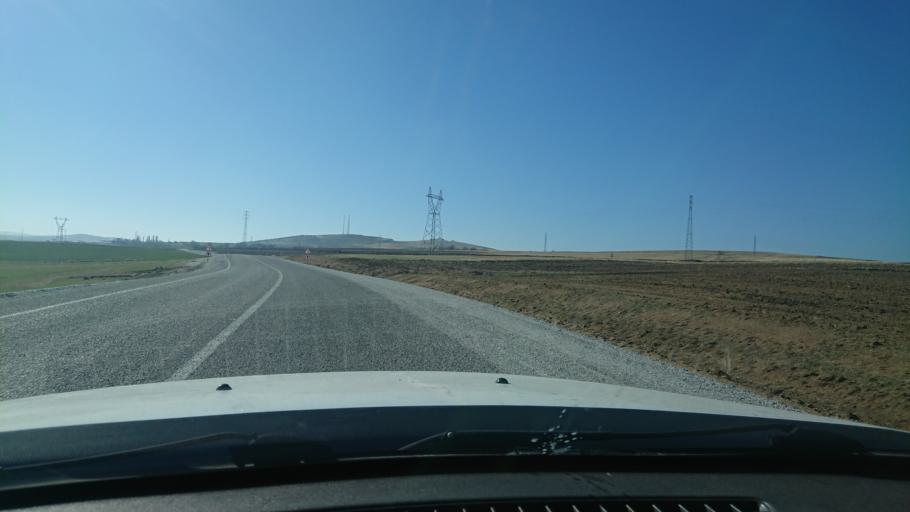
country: TR
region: Aksaray
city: Agacoren
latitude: 38.8956
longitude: 33.9308
